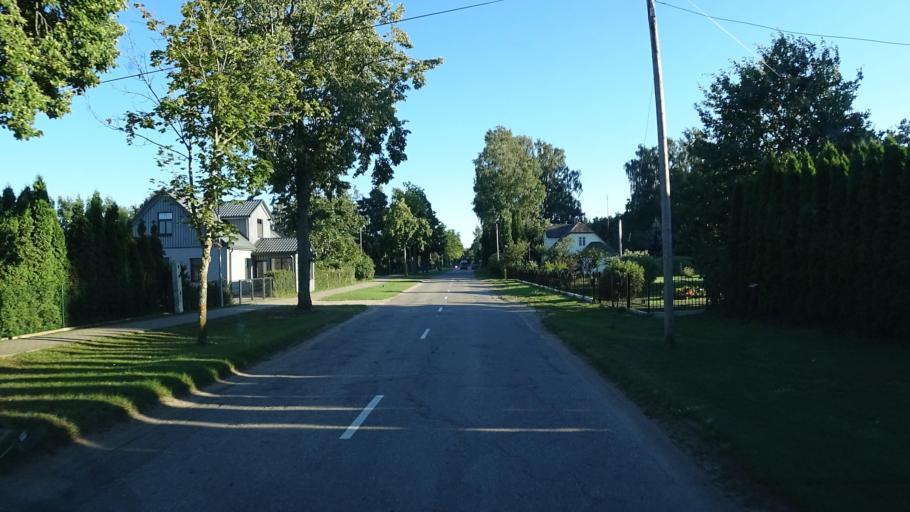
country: LV
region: Dundaga
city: Dundaga
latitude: 57.7416
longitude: 22.5837
